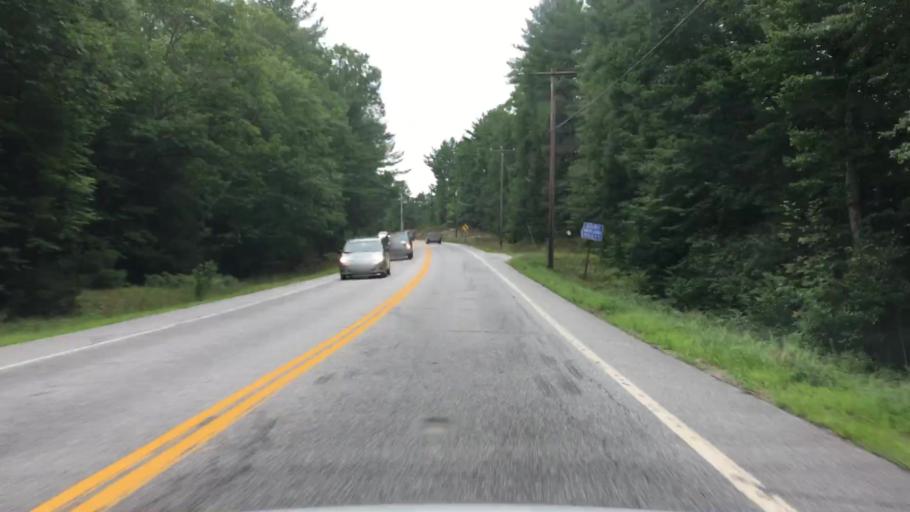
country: US
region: Maine
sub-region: Oxford County
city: Hiram
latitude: 43.8564
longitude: -70.7905
